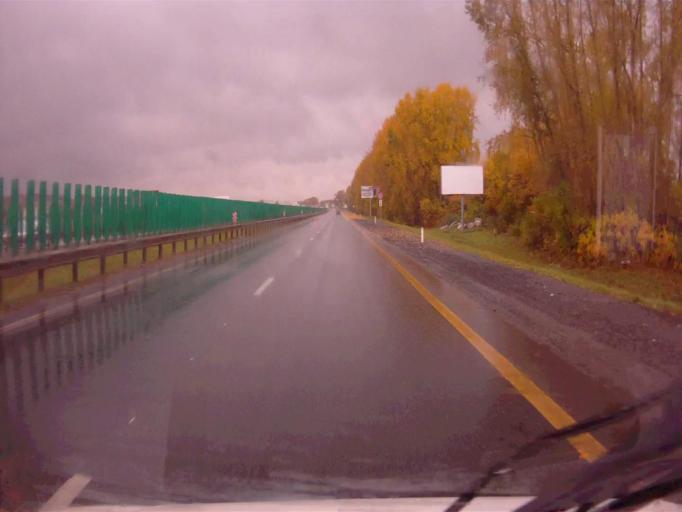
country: RU
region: Chelyabinsk
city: Dolgoderevenskoye
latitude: 55.2786
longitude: 61.3435
